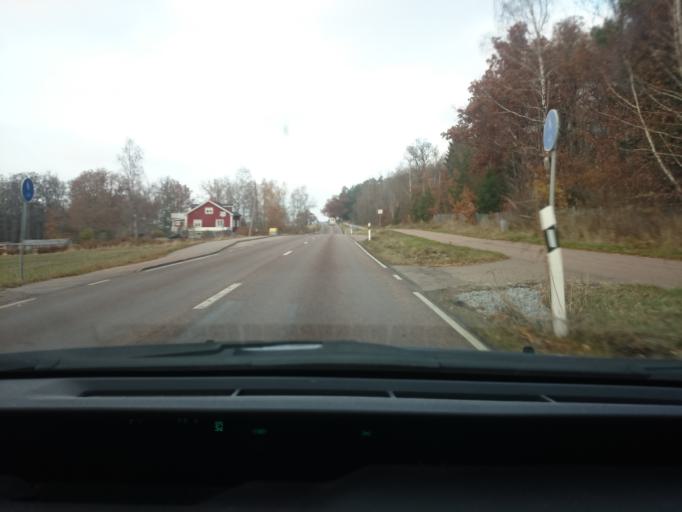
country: SE
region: Vaestmanland
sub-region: Vasteras
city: Skultuna
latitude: 59.6728
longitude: 16.4722
